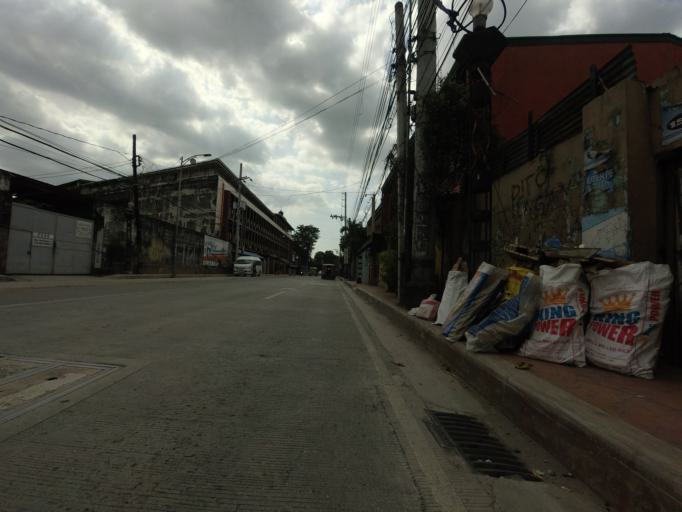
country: PH
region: Metro Manila
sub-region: San Juan
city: San Juan
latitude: 14.5829
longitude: 121.0145
